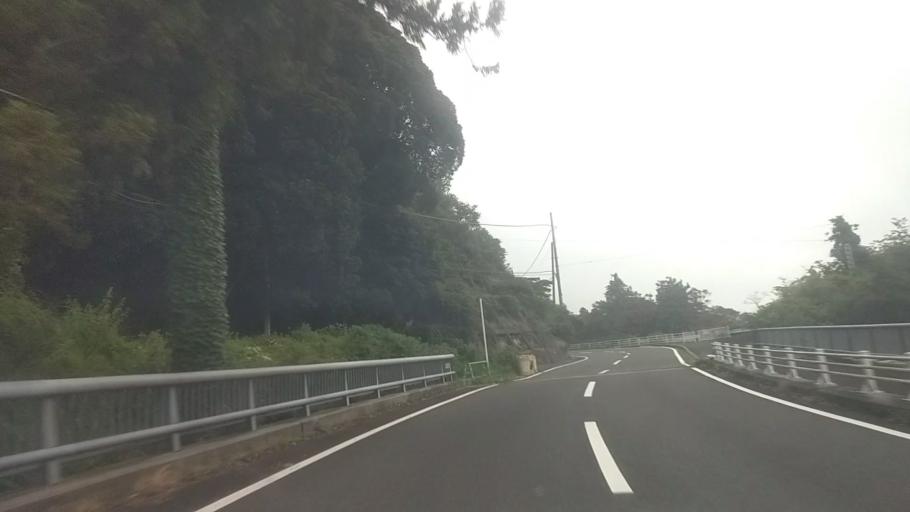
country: JP
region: Chiba
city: Kawaguchi
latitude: 35.1425
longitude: 140.1499
